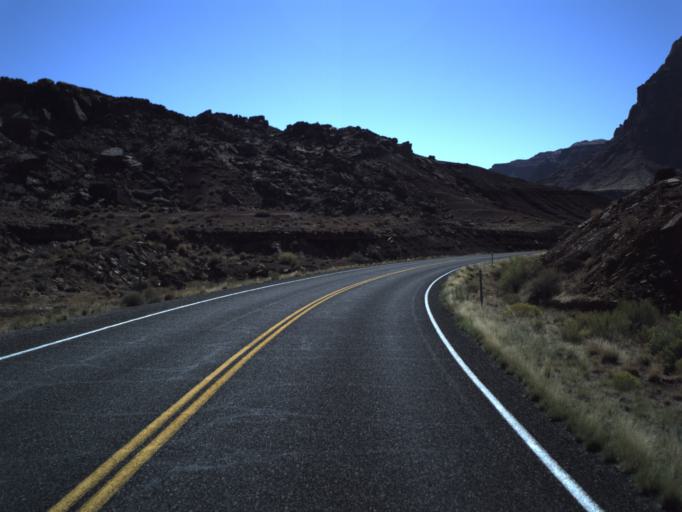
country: US
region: Utah
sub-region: San Juan County
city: Blanding
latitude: 37.9038
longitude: -110.4509
